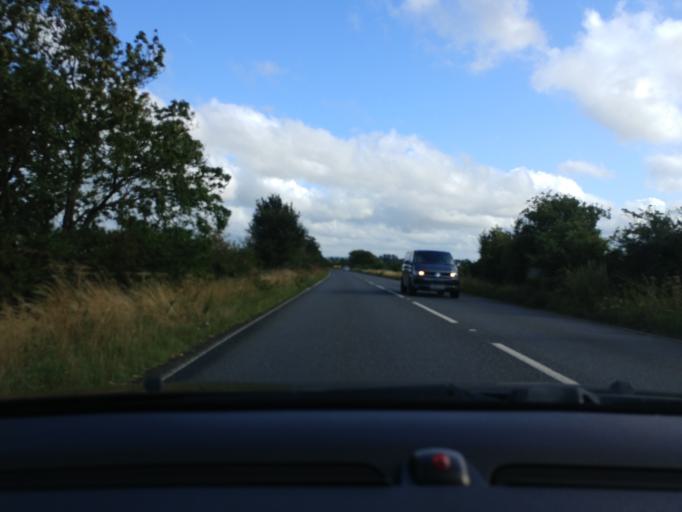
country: GB
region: England
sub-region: Oxfordshire
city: Kidlington
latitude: 51.8761
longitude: -1.2301
